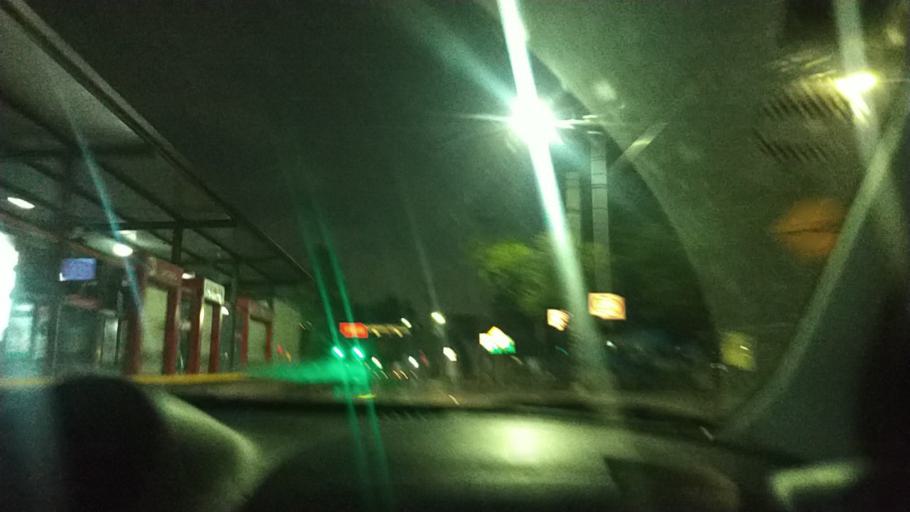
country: MX
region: Mexico
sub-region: Tultitlan
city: Buenavista
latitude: 19.5997
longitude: -99.1835
